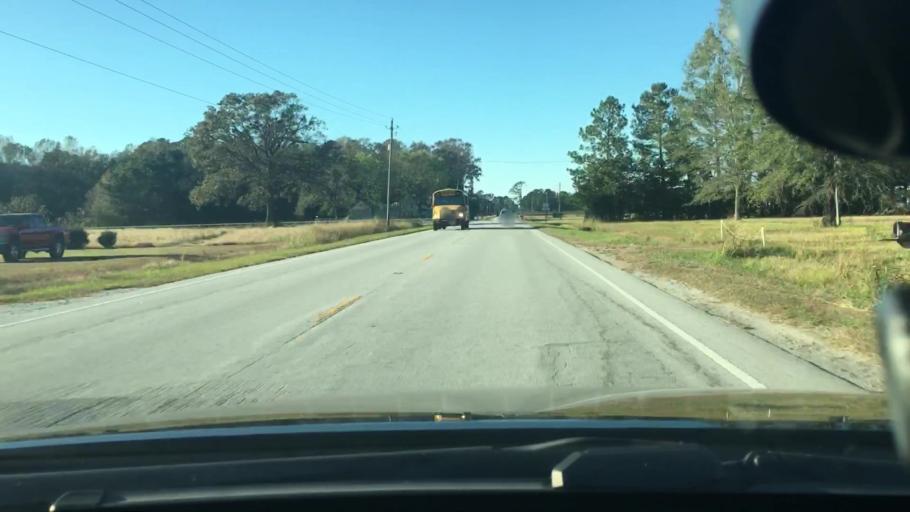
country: US
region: North Carolina
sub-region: Craven County
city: Vanceboro
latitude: 35.3492
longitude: -77.1861
